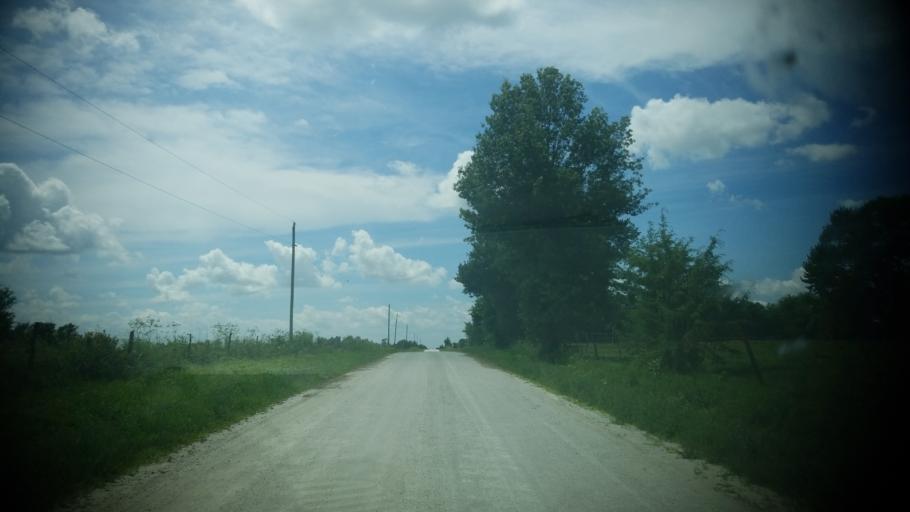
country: US
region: Missouri
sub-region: Pike County
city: Bowling Green
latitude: 39.3084
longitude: -91.3071
